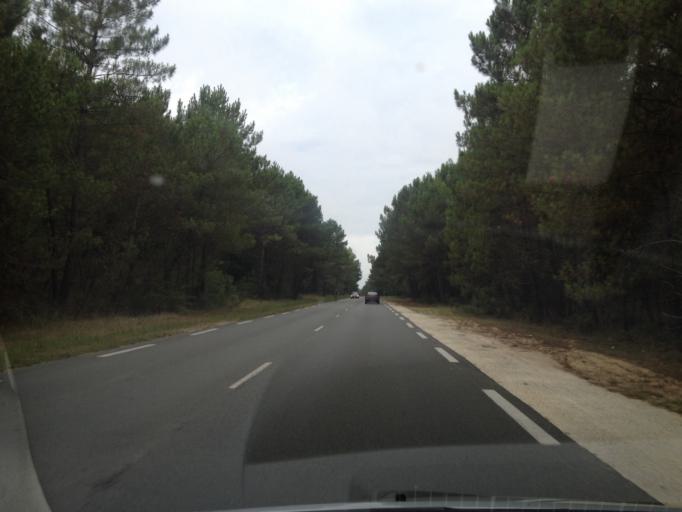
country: FR
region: Poitou-Charentes
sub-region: Departement de la Charente-Maritime
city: Saint-Palais-sur-Mer
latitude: 45.6616
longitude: -1.0801
